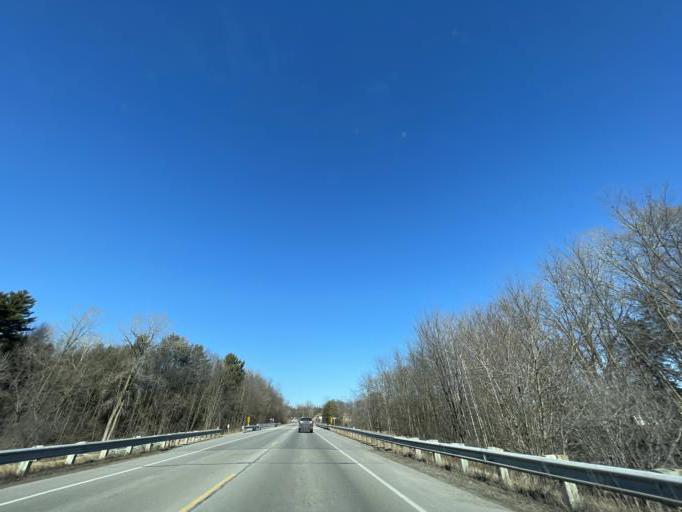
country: US
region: Wisconsin
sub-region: Brown County
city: Suamico
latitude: 44.6318
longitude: -88.0542
